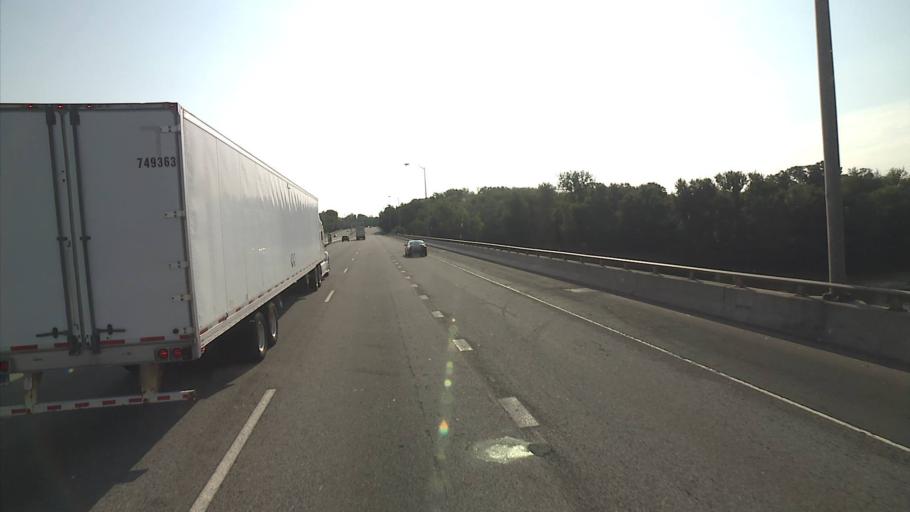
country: US
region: Connecticut
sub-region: Hartford County
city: Windsor Locks
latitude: 41.9169
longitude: -72.6228
